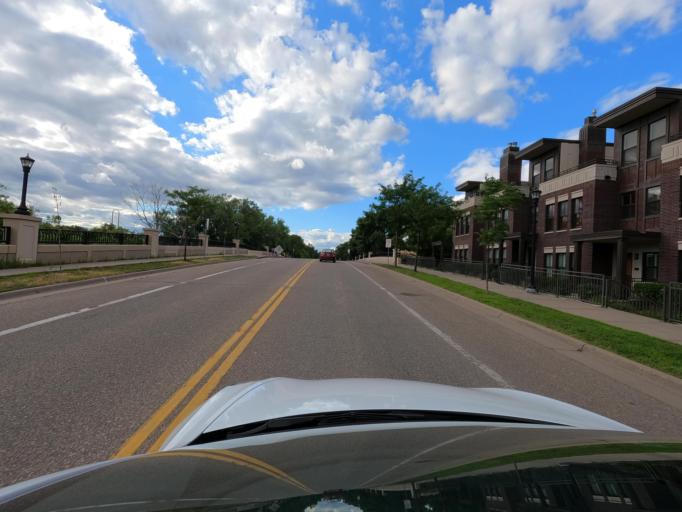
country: US
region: Minnesota
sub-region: Hennepin County
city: Minneapolis
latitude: 44.9886
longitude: -93.2604
